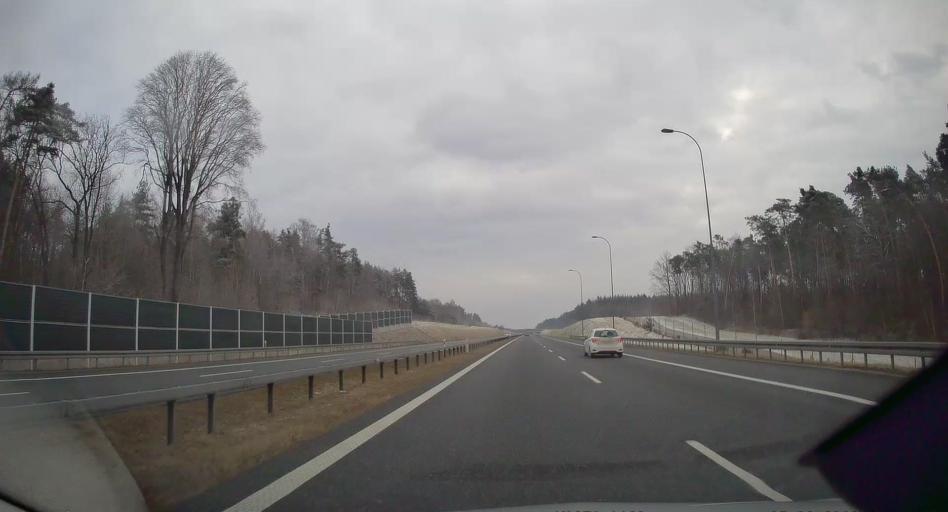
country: PL
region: Lesser Poland Voivodeship
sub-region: Powiat brzeski
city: Brzesko
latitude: 50.0009
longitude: 20.6326
